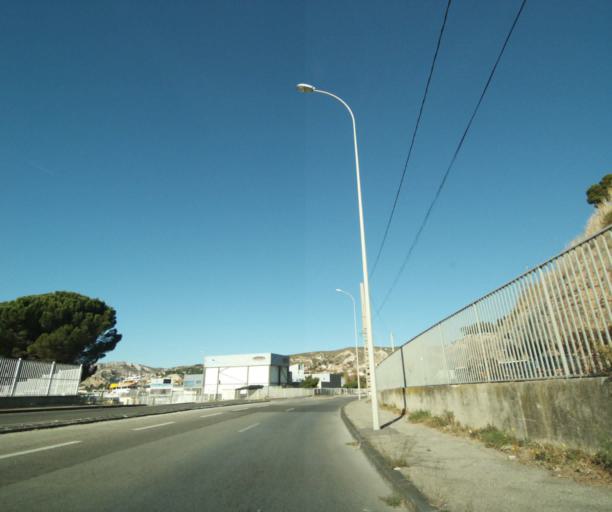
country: FR
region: Provence-Alpes-Cote d'Azur
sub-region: Departement des Bouches-du-Rhone
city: Marseille 16
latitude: 43.3541
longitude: 5.3282
